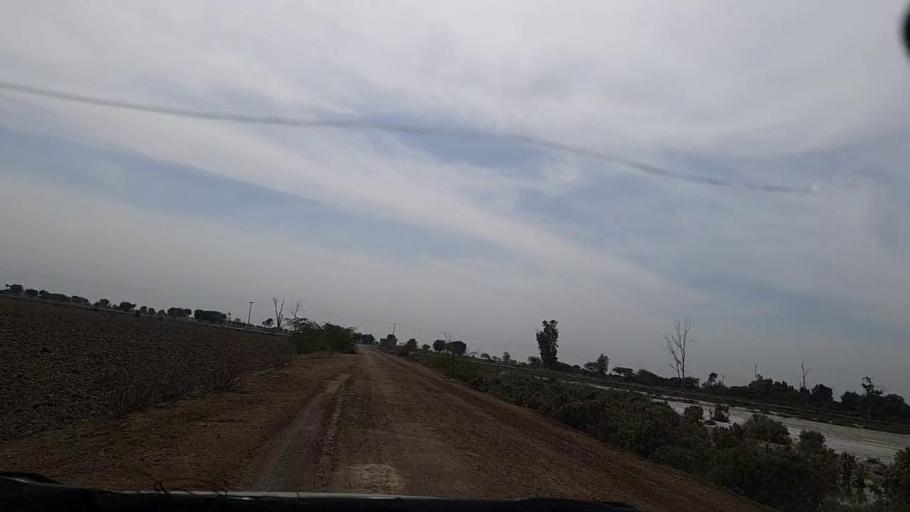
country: PK
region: Sindh
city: Dhoro Naro
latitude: 25.4434
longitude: 69.4919
